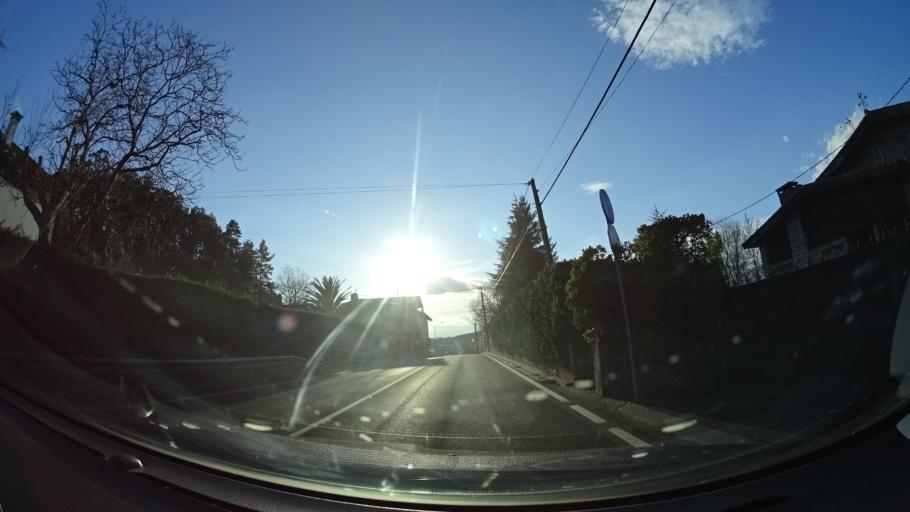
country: ES
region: Basque Country
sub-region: Bizkaia
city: Mungia
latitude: 43.3718
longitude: -2.8038
